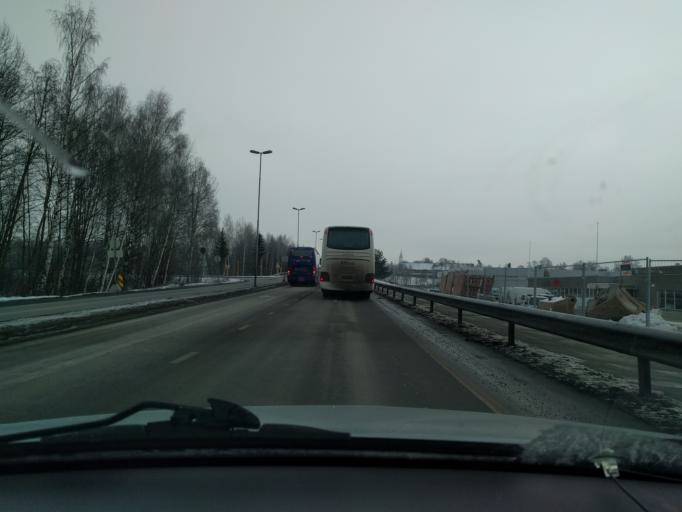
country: NO
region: Hedmark
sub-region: Hamar
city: Hamar
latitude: 60.7990
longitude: 11.1125
